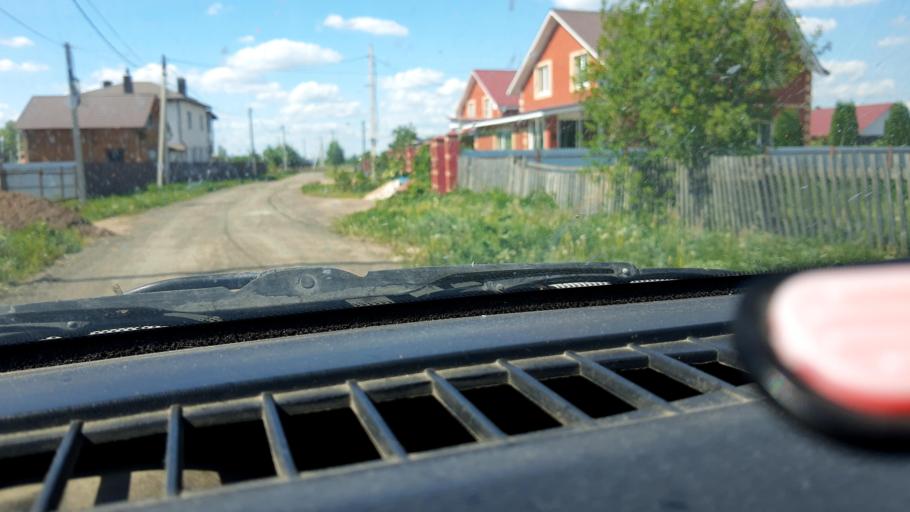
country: RU
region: Bashkortostan
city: Kabakovo
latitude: 54.6838
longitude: 56.1334
